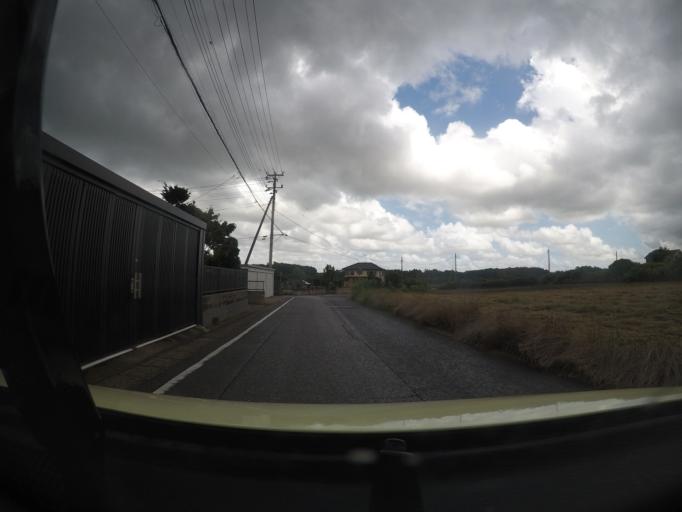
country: JP
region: Ibaraki
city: Iwai
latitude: 36.0438
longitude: 139.9011
